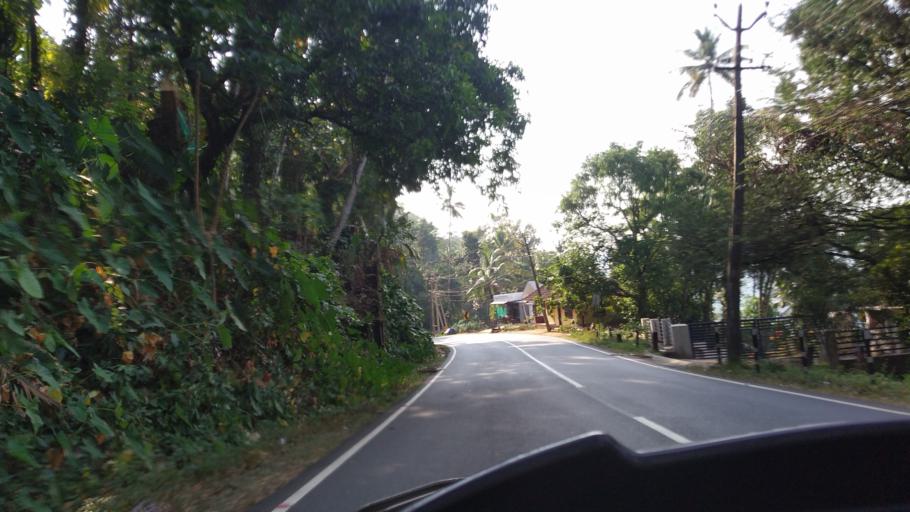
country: IN
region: Kerala
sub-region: Kottayam
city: Erattupetta
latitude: 9.5544
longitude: 76.9211
